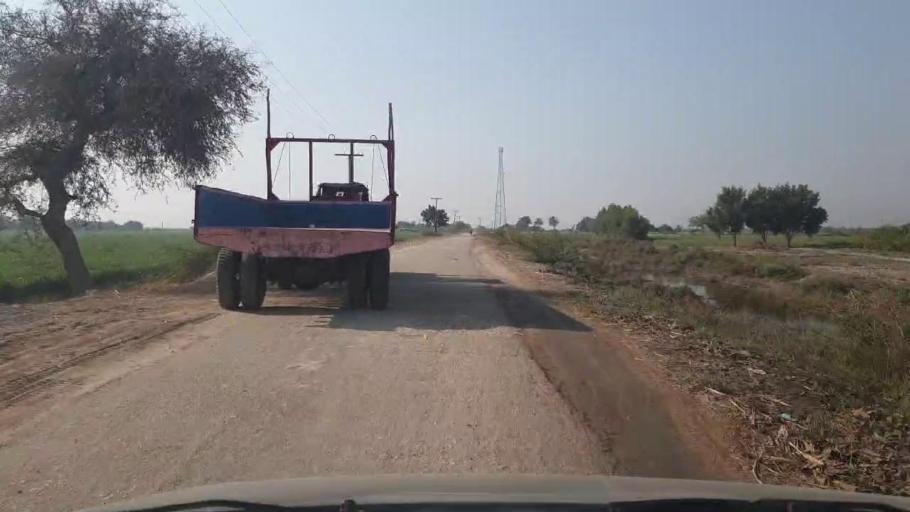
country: PK
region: Sindh
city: Mirwah Gorchani
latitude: 25.2989
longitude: 69.1475
